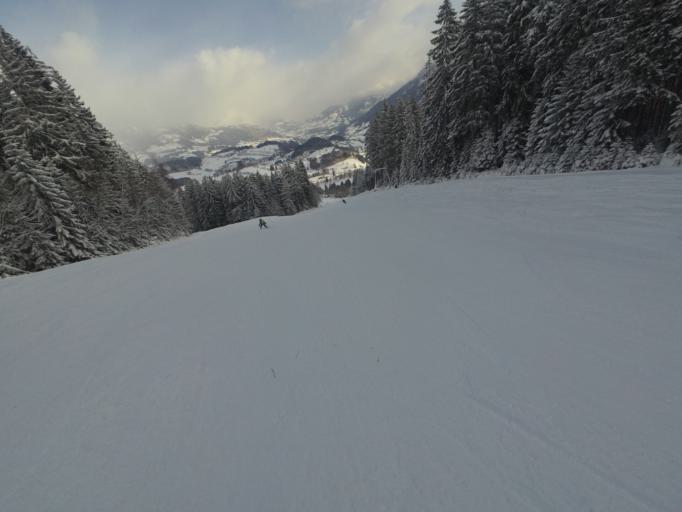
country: AT
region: Salzburg
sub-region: Politischer Bezirk Zell am See
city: Lend
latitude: 47.3092
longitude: 13.0670
